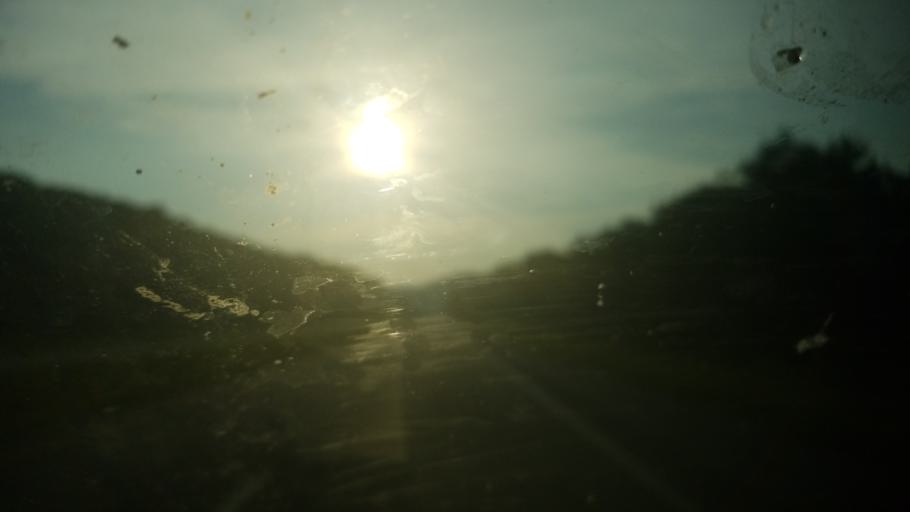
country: US
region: Ohio
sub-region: Pike County
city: Piketon
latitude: 39.0444
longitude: -83.1714
